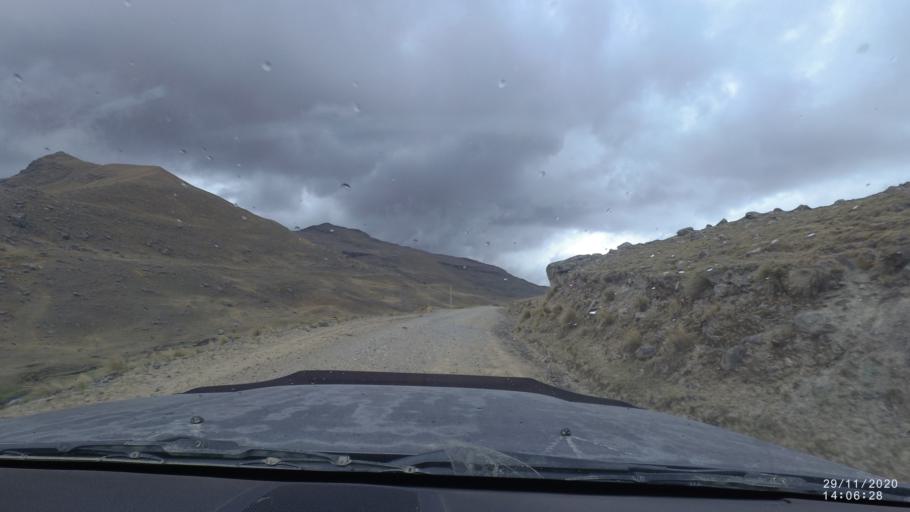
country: BO
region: Cochabamba
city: Sipe Sipe
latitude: -17.2141
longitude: -66.3785
